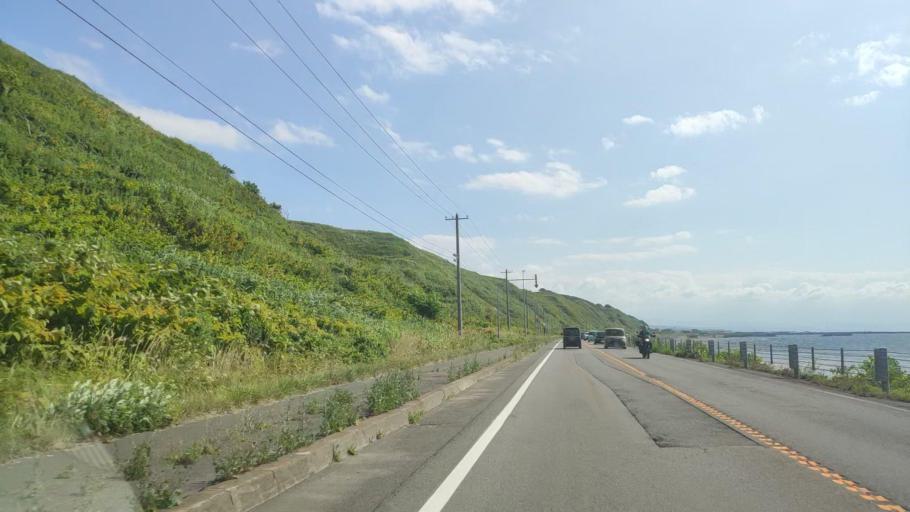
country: JP
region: Hokkaido
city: Rumoi
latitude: 43.9933
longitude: 141.6514
